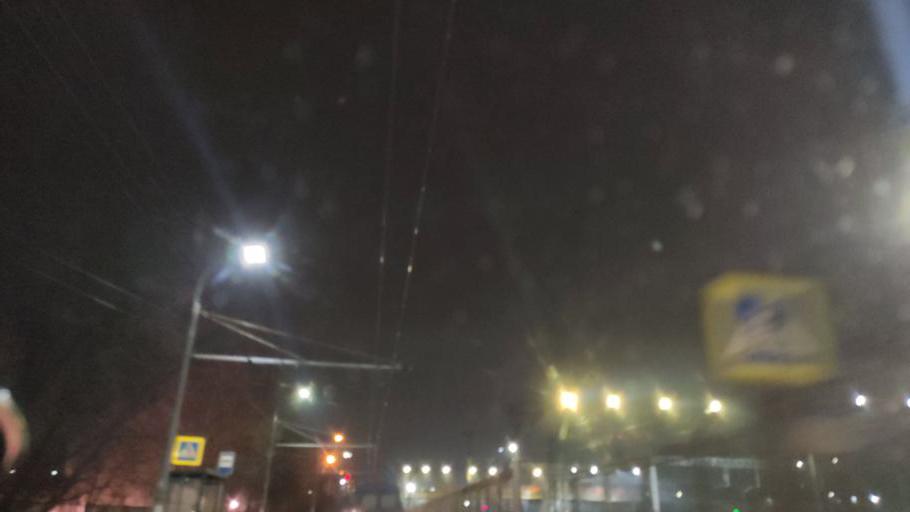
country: RU
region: Moskovskaya
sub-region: Podol'skiy Rayon
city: Podol'sk
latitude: 55.4269
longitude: 37.5636
